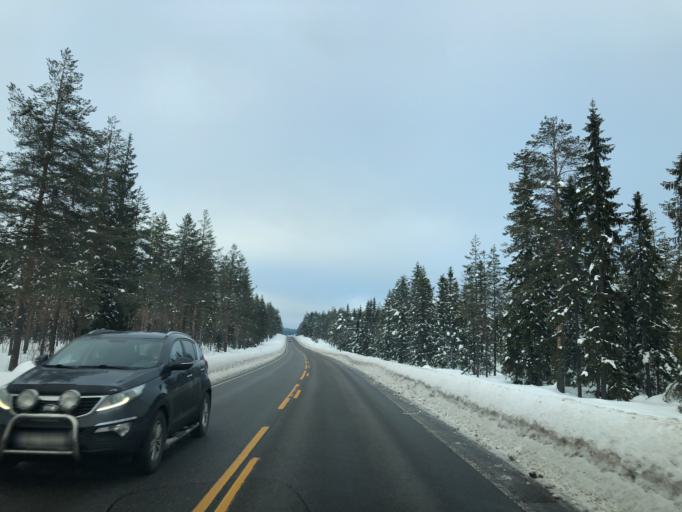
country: NO
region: Hedmark
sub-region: Trysil
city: Innbygda
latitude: 61.2038
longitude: 12.2208
